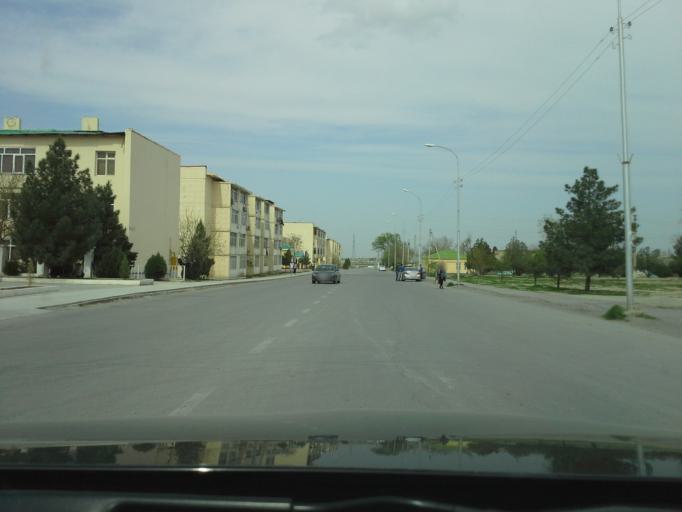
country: TM
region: Ahal
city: Abadan
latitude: 38.0590
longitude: 58.1504
